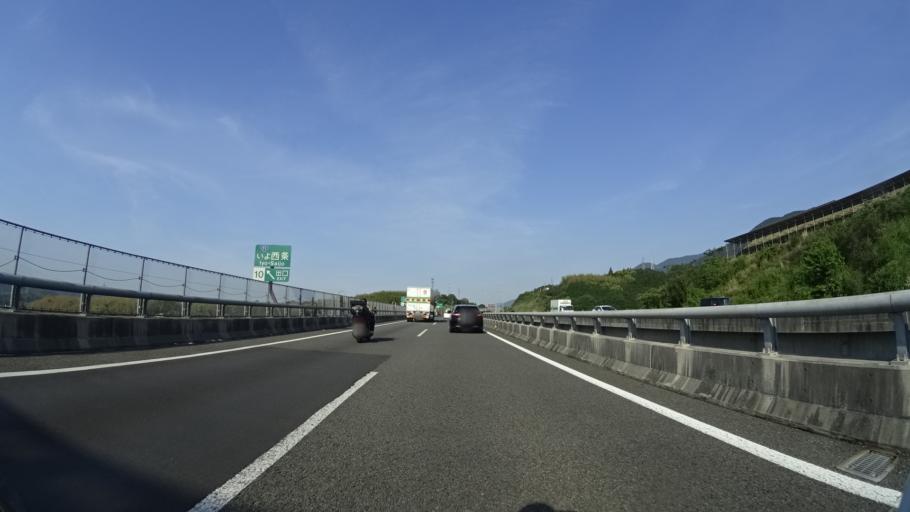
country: JP
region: Ehime
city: Saijo
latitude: 33.9117
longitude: 133.2330
